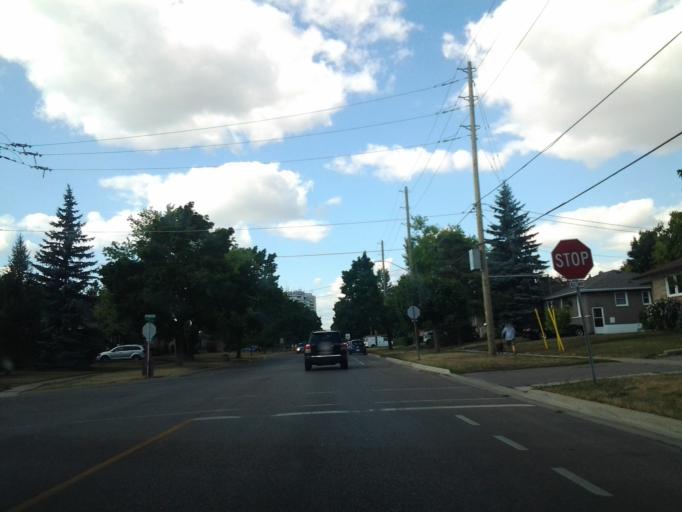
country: CA
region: Ontario
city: Brampton
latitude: 43.6455
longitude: -79.8811
